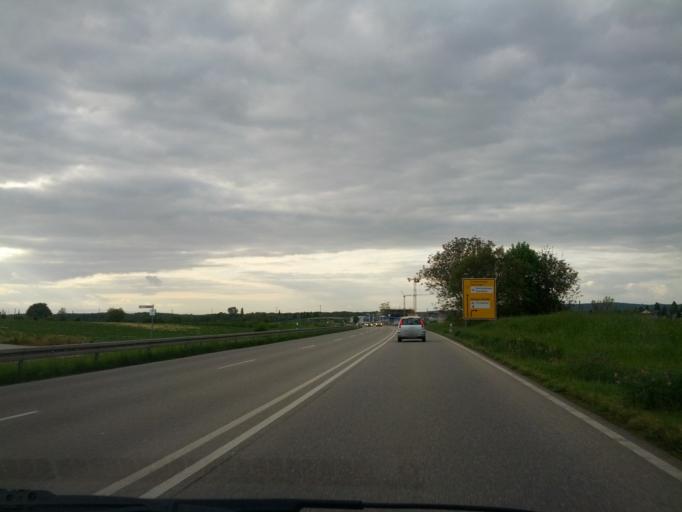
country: DE
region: Baden-Wuerttemberg
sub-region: Freiburg Region
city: Denzlingen
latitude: 48.0619
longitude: 7.8706
